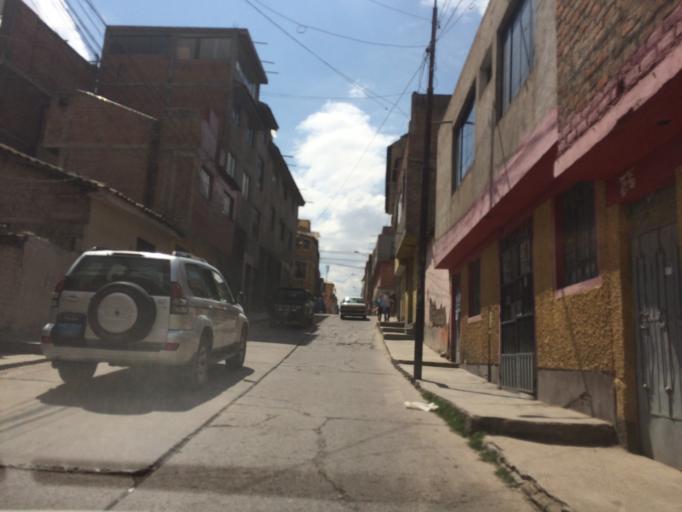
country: PE
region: Ayacucho
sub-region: Provincia de Huamanga
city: Ayacucho
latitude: -13.1586
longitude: -74.2222
